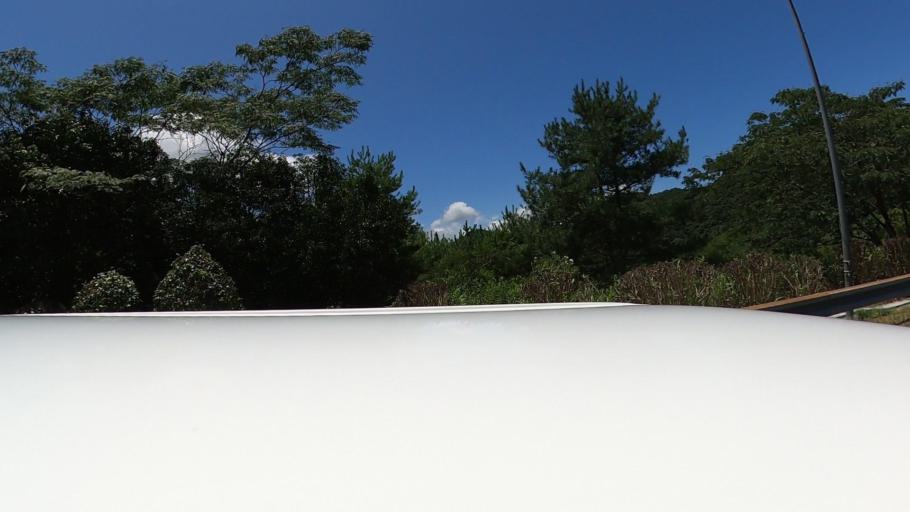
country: JP
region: Miyazaki
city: Nobeoka
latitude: 32.5223
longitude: 131.6650
